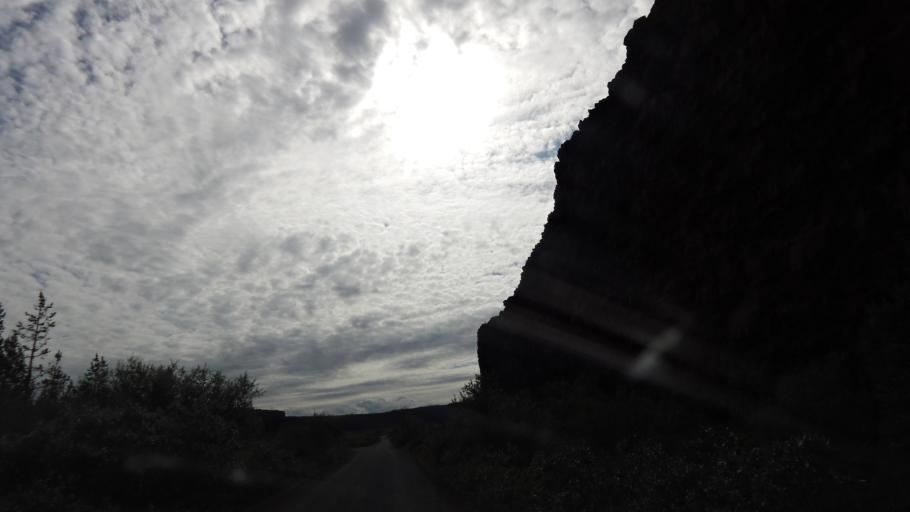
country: IS
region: Northeast
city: Husavik
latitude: 66.0141
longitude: -16.5013
